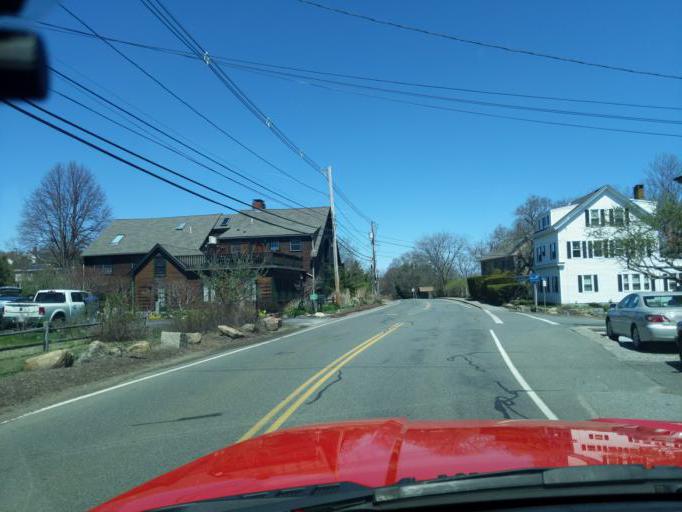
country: US
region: Massachusetts
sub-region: Essex County
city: Rockport
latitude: 42.6670
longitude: -70.6252
